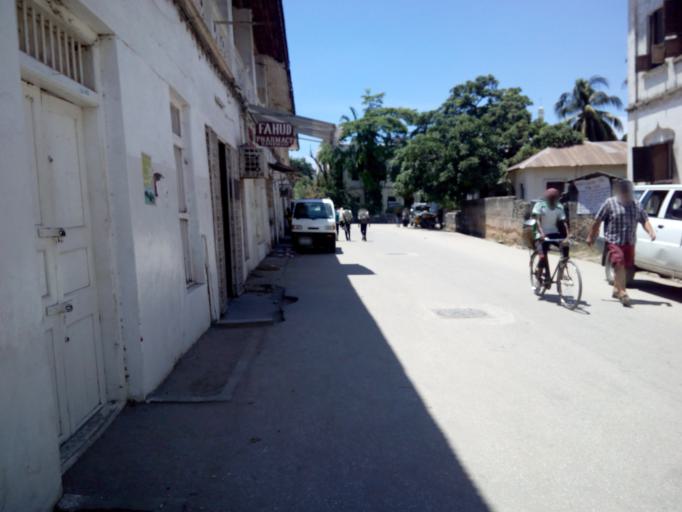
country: TZ
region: Zanzibar Urban/West
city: Zanzibar
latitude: -6.1640
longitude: 39.1930
